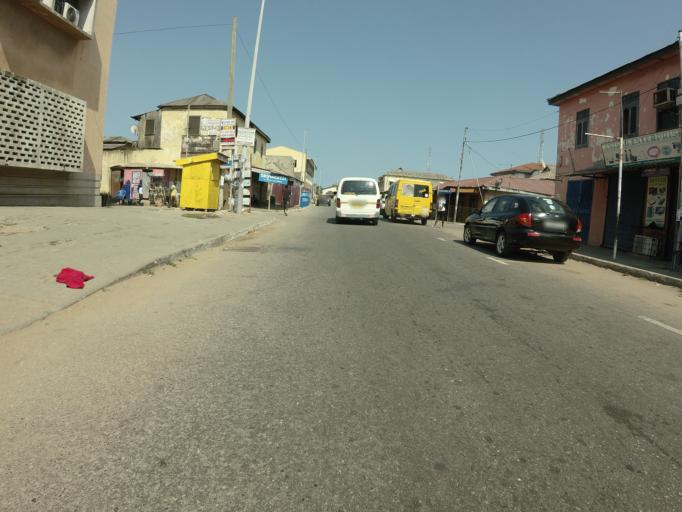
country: GH
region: Greater Accra
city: Accra
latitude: 5.5410
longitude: -0.2084
